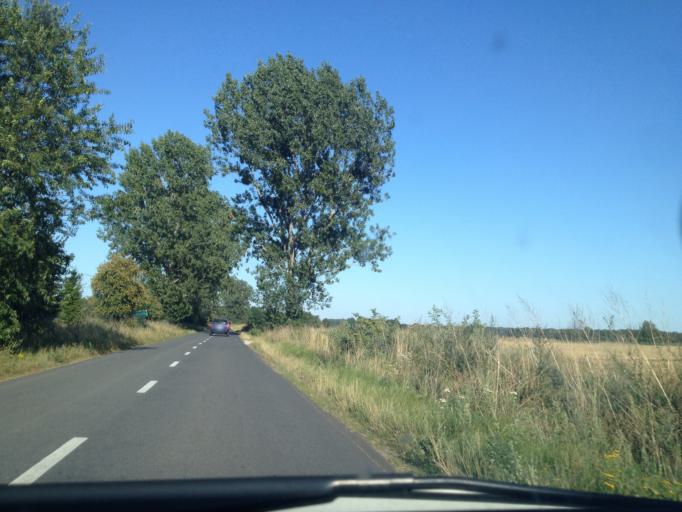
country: PL
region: Greater Poland Voivodeship
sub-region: Powiat sremski
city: Srem
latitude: 52.1108
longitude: 17.0793
